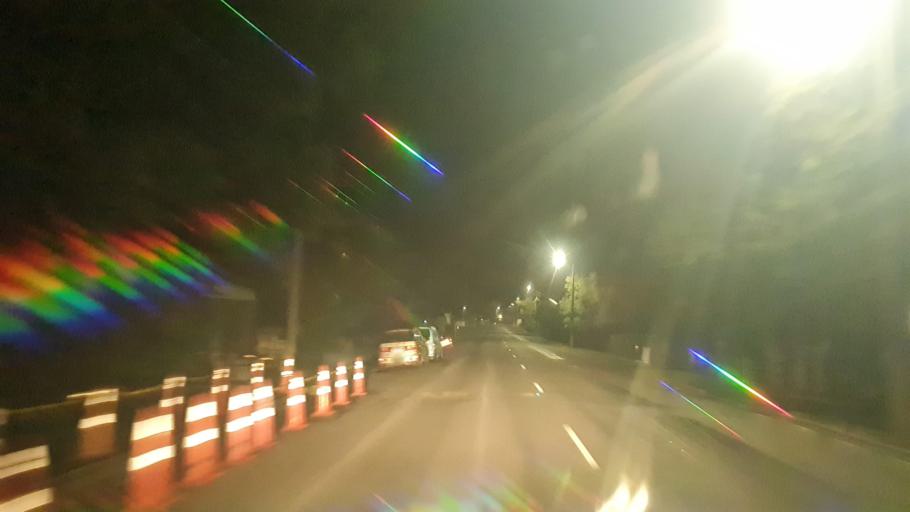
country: NZ
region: Otago
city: Oamaru
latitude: -45.0978
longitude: 170.9609
